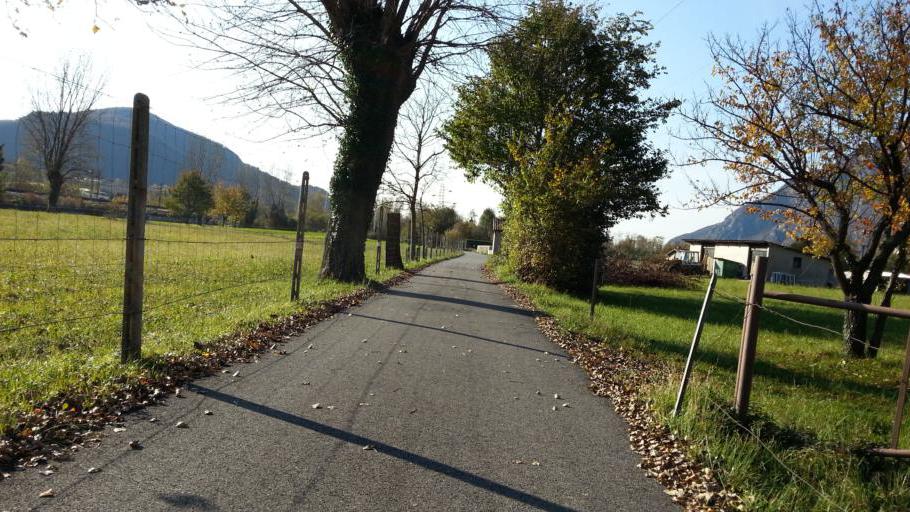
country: IT
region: Friuli Venezia Giulia
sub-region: Provincia di Udine
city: Venzone
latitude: 46.3288
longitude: 13.1320
